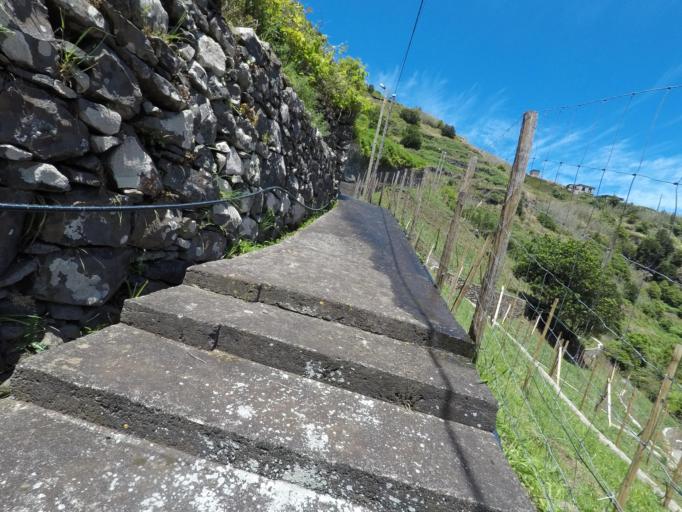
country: PT
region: Madeira
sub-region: Sao Vicente
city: Sao Vicente
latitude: 32.8230
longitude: -16.9786
